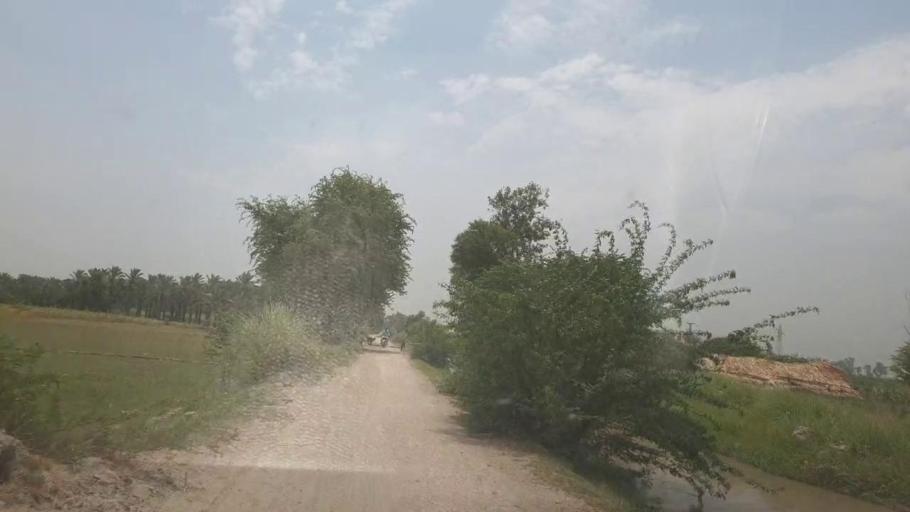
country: PK
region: Sindh
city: Kot Diji
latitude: 27.4440
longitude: 68.6765
